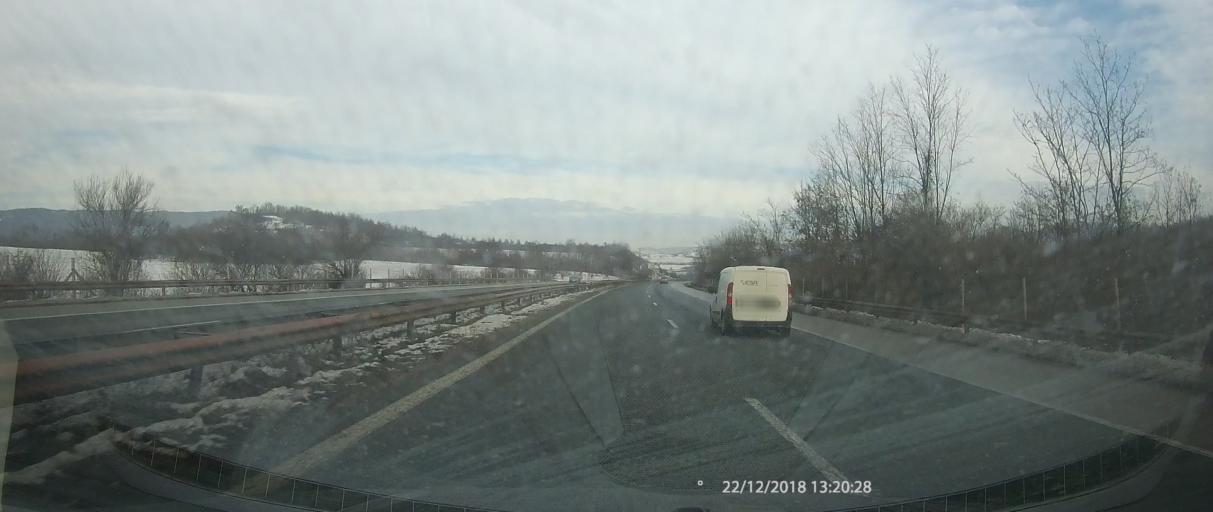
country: BG
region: Lovech
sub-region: Obshtina Yablanitsa
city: Yablanitsa
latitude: 42.9577
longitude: 24.0247
